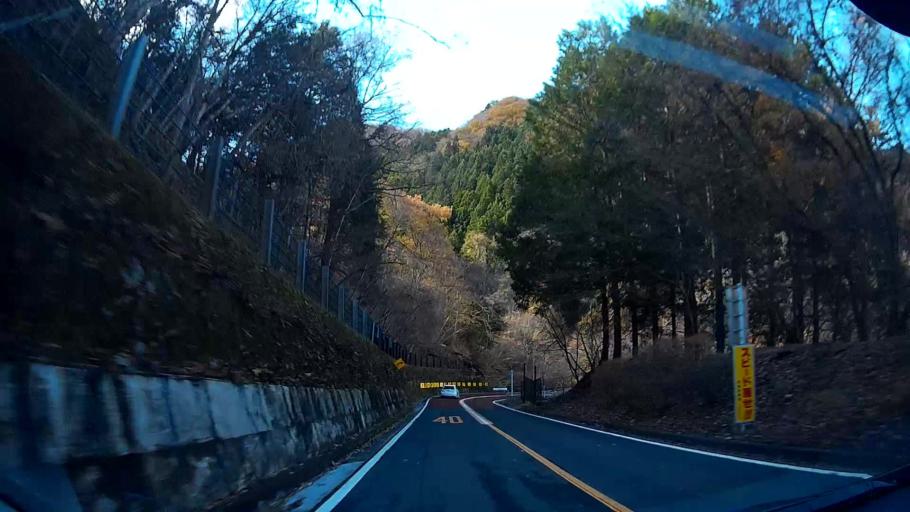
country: JP
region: Yamanashi
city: Uenohara
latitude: 35.7606
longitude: 139.0222
